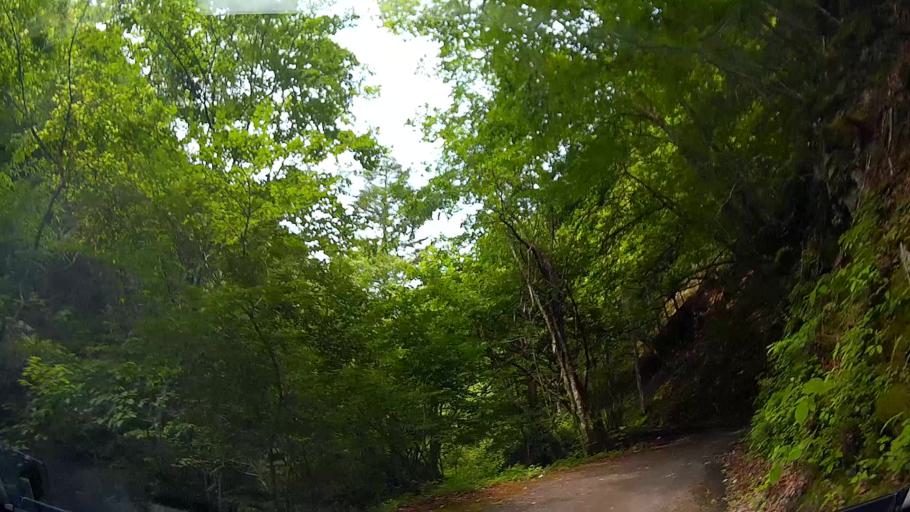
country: JP
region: Nagano
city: Iida
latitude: 35.4674
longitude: 138.0004
